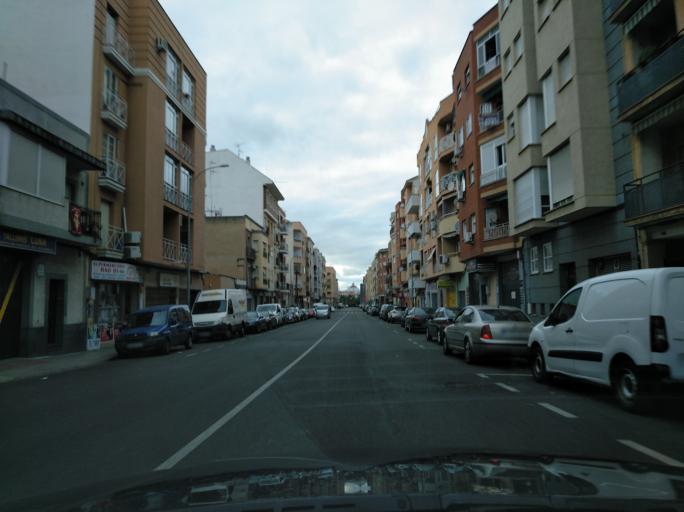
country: ES
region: Extremadura
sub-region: Provincia de Badajoz
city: Badajoz
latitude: 38.8760
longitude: -6.9566
